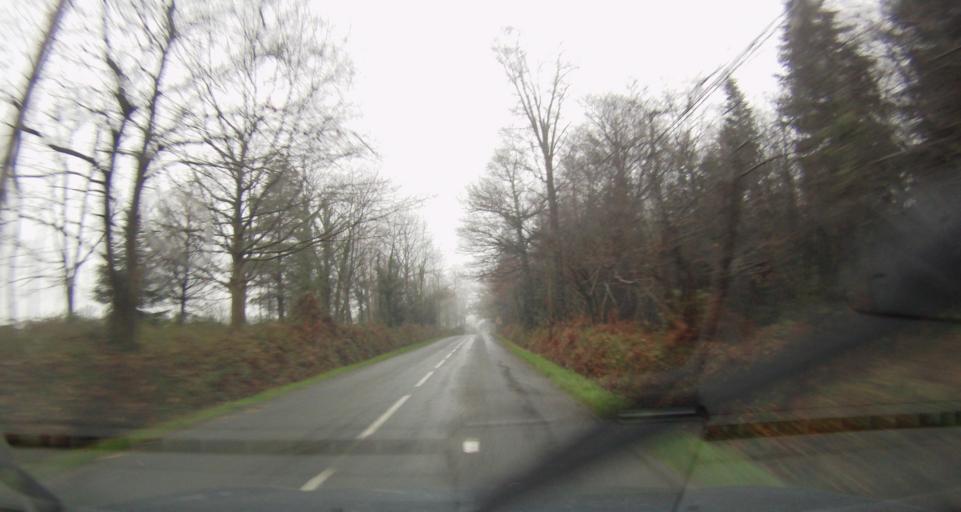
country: FR
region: Brittany
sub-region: Departement d'Ille-et-Vilaine
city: Orgeres
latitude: 47.9752
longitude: -1.6853
